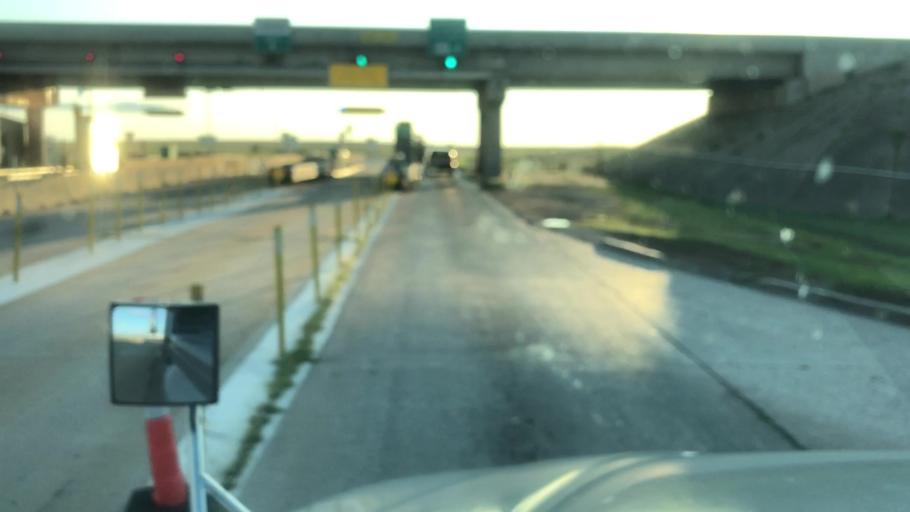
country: US
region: Oklahoma
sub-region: Noble County
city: Perry
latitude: 36.3837
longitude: -97.0671
